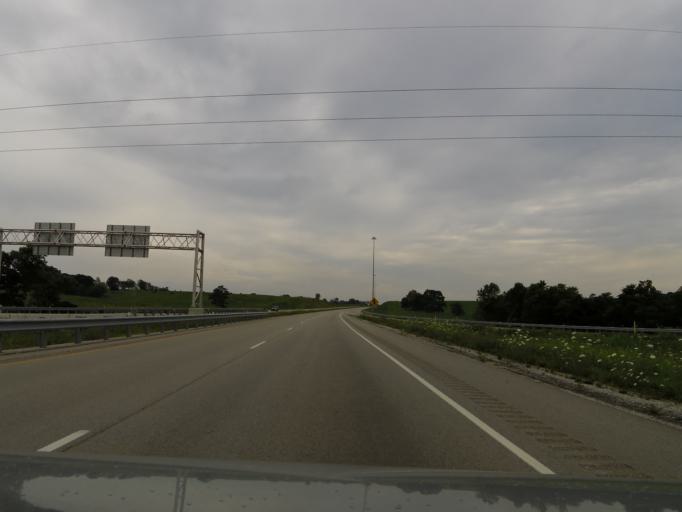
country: US
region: Ohio
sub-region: Brown County
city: Aberdeen
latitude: 38.6388
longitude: -83.8325
